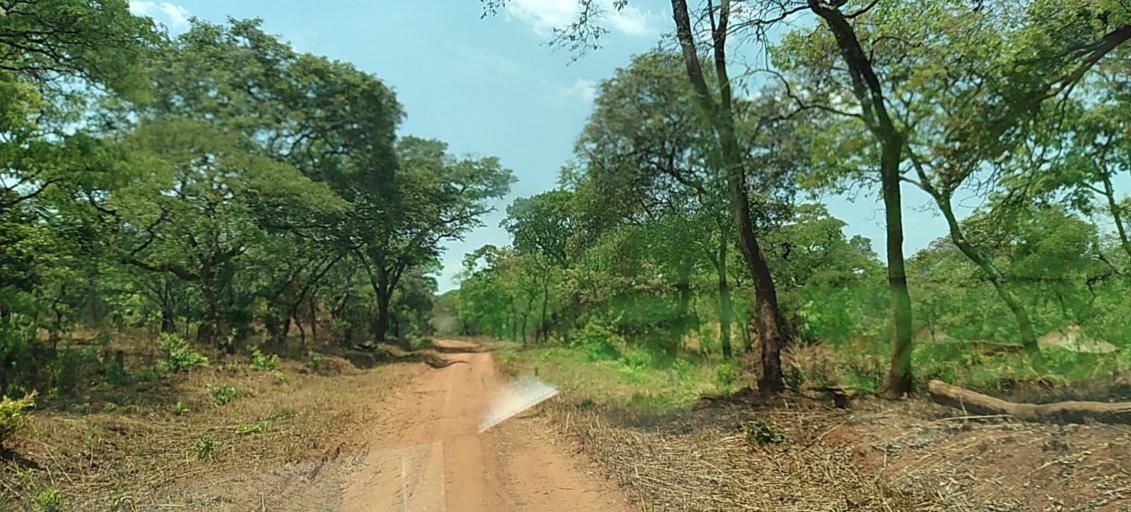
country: CD
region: Katanga
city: Kolwezi
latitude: -11.3584
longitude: 25.2071
